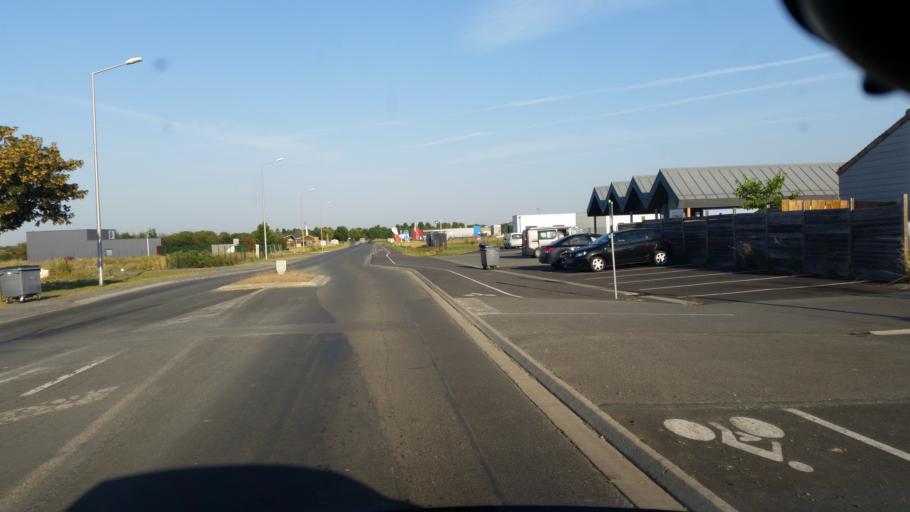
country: FR
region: Poitou-Charentes
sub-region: Departement de la Charente-Maritime
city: Saint-Jean-de-Liversay
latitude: 46.2272
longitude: -0.8690
